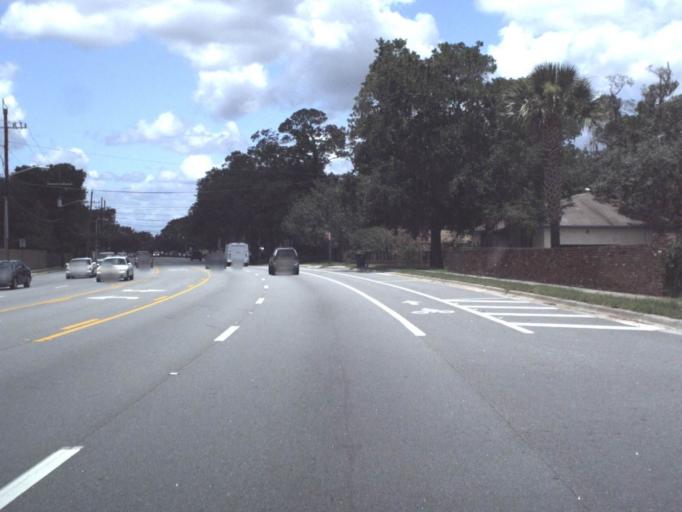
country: US
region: Florida
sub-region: Clay County
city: Orange Park
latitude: 30.2230
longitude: -81.6155
